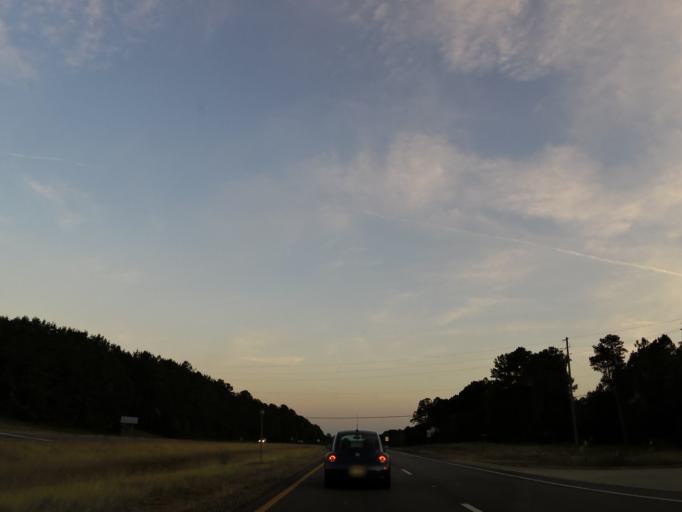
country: US
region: Mississippi
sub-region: Kemper County
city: De Kalb
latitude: 32.8303
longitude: -88.4625
